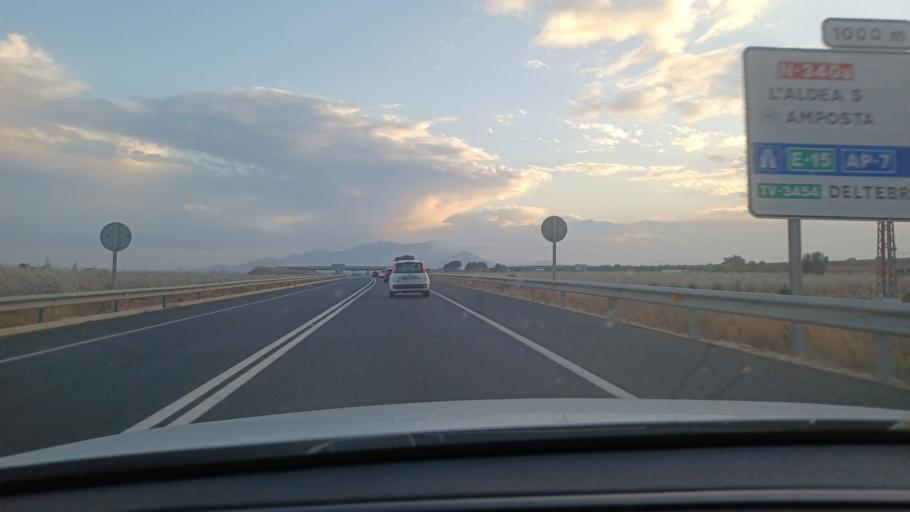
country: ES
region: Catalonia
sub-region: Provincia de Tarragona
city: Amposta
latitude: 40.7422
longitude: 0.5942
